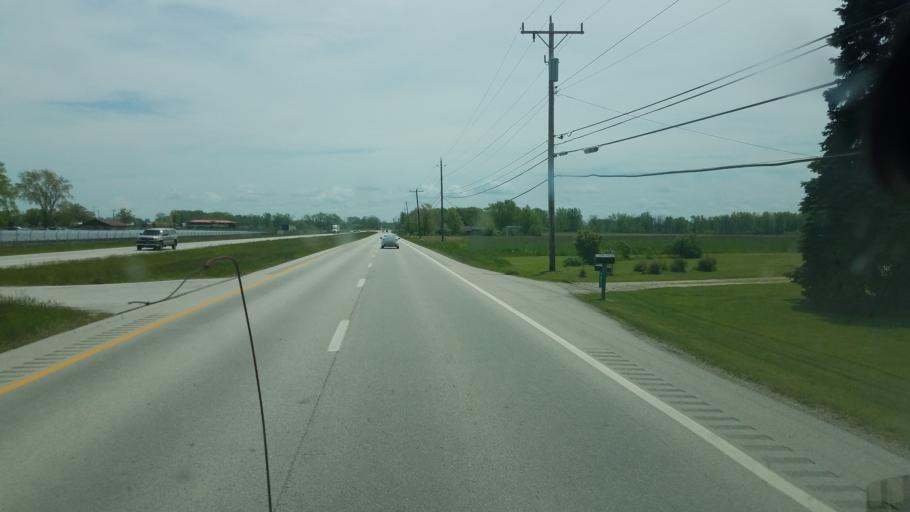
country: US
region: Ohio
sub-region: Ottawa County
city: Port Clinton
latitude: 41.5337
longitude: -83.0280
